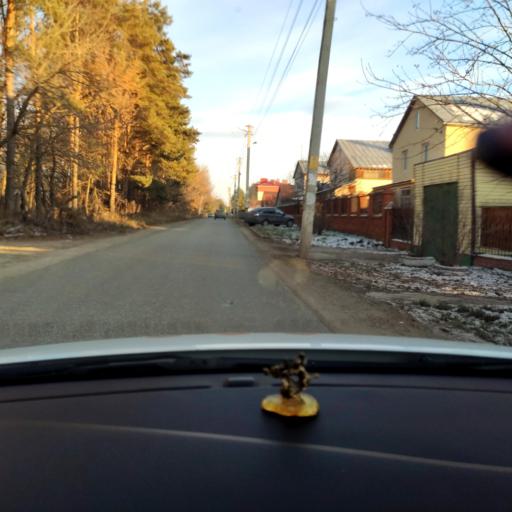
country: RU
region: Tatarstan
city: Stolbishchi
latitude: 55.6126
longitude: 49.1326
